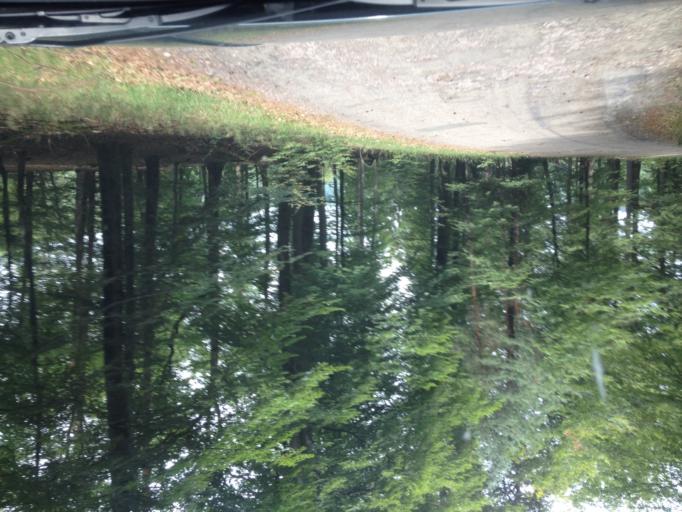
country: DE
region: Rheinland-Pfalz
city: Wilgartswiesen
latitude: 49.2929
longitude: 7.8953
